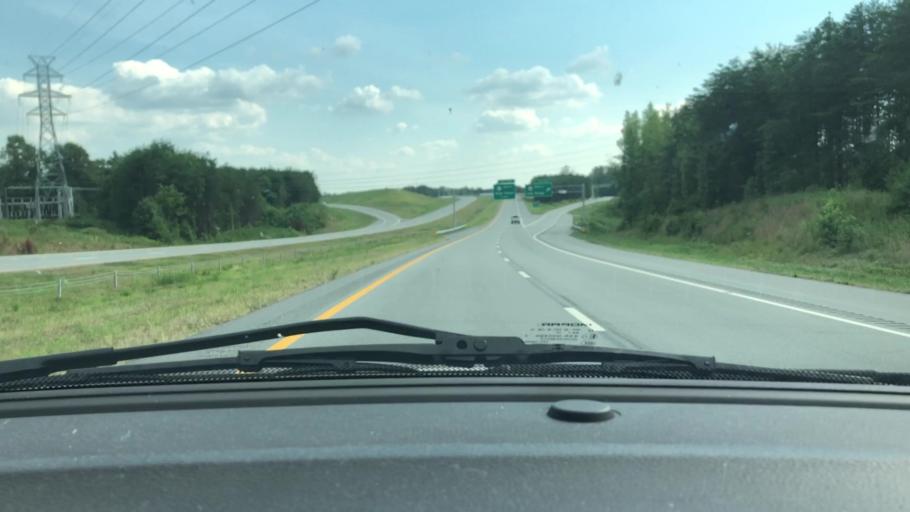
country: US
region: North Carolina
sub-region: Guilford County
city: Oak Ridge
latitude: 36.1404
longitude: -79.9606
